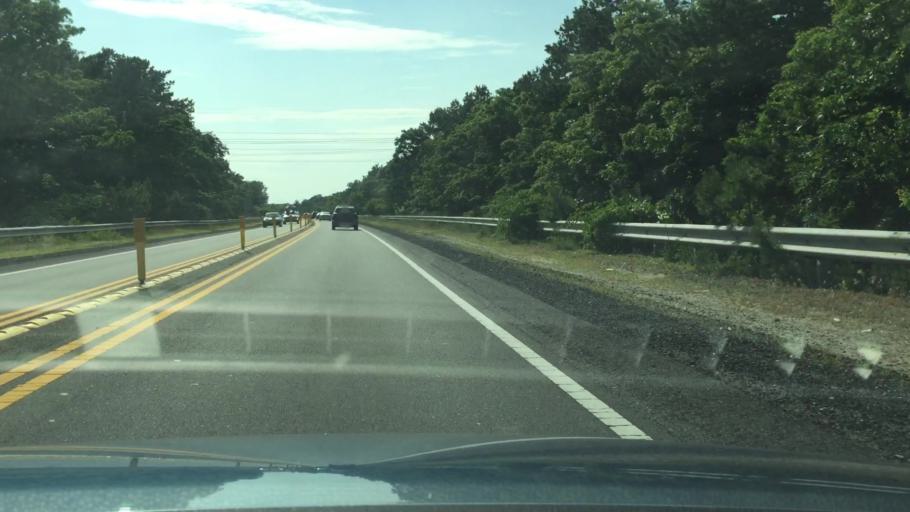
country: US
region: Massachusetts
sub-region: Barnstable County
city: Northwest Harwich
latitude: 41.7007
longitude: -70.1135
